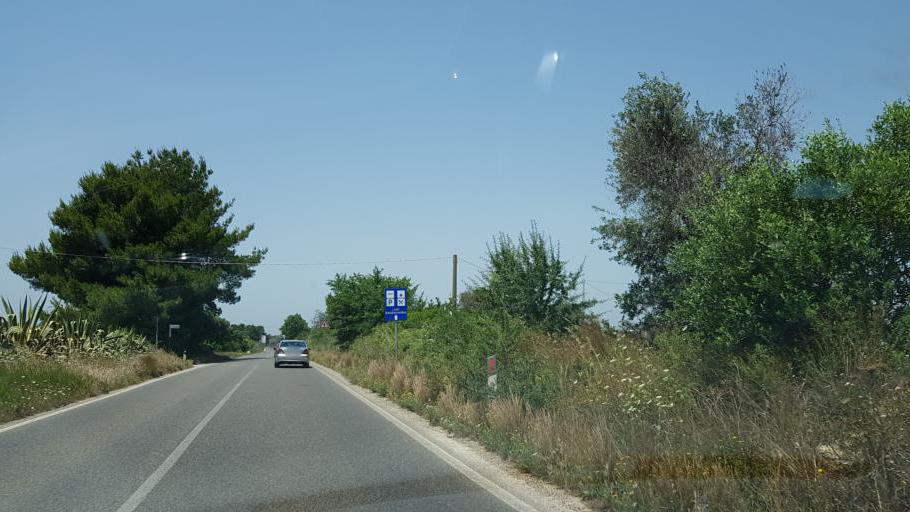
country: IT
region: Apulia
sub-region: Provincia di Lecce
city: Porto Cesareo
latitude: 40.2711
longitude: 17.9051
